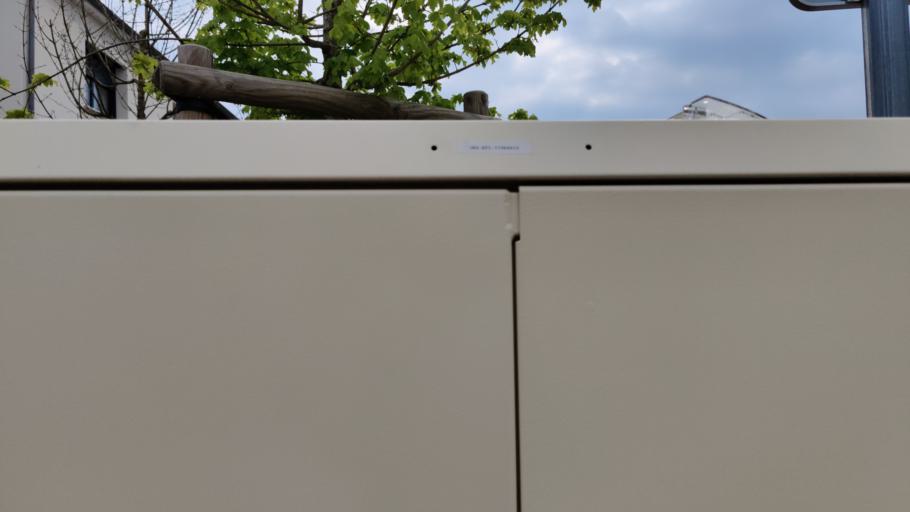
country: FR
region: Centre
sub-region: Departement du Loiret
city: Saint-Jean-le-Blanc
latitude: 47.8884
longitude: 1.9347
